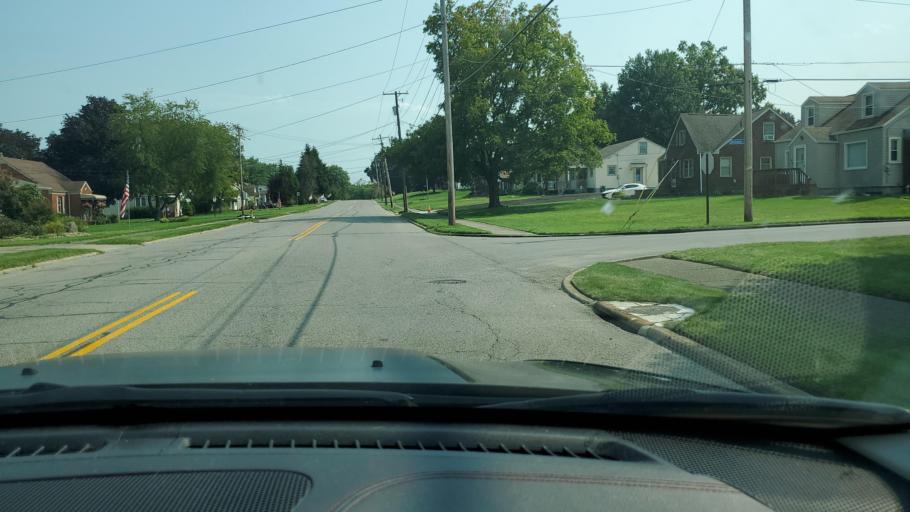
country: US
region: Ohio
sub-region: Mahoning County
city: Struthers
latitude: 41.0419
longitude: -80.6035
